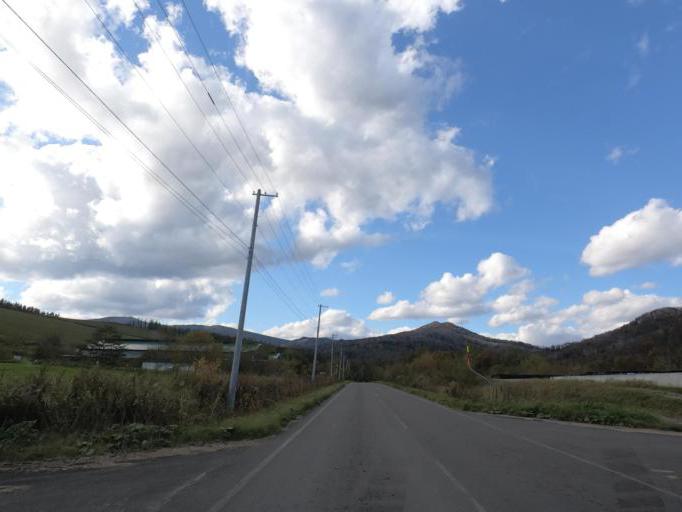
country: JP
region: Hokkaido
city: Otofuke
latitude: 43.2892
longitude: 143.2298
